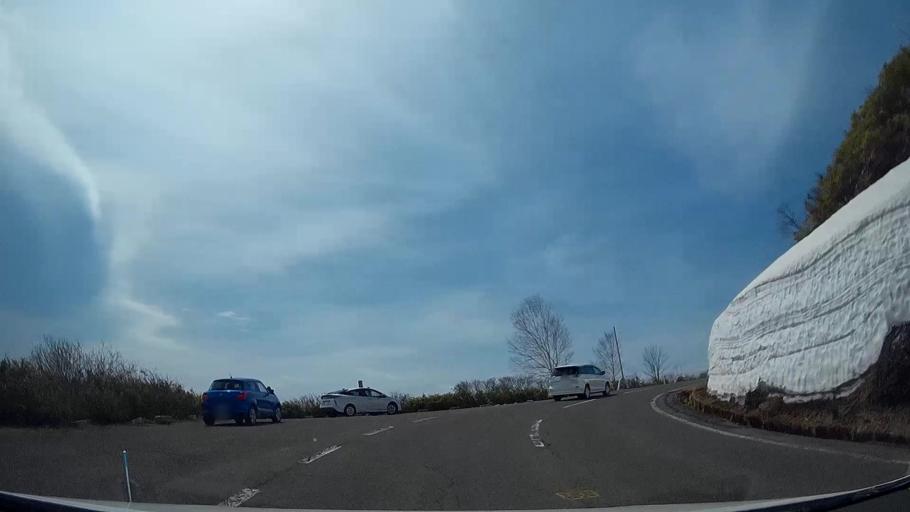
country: JP
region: Iwate
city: Shizukuishi
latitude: 39.9379
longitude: 140.9180
